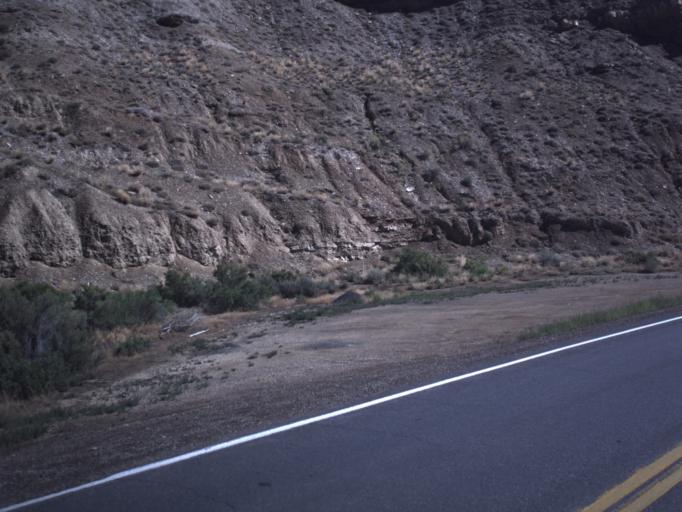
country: US
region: Utah
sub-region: Duchesne County
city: Duchesne
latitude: 40.1550
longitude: -110.4108
